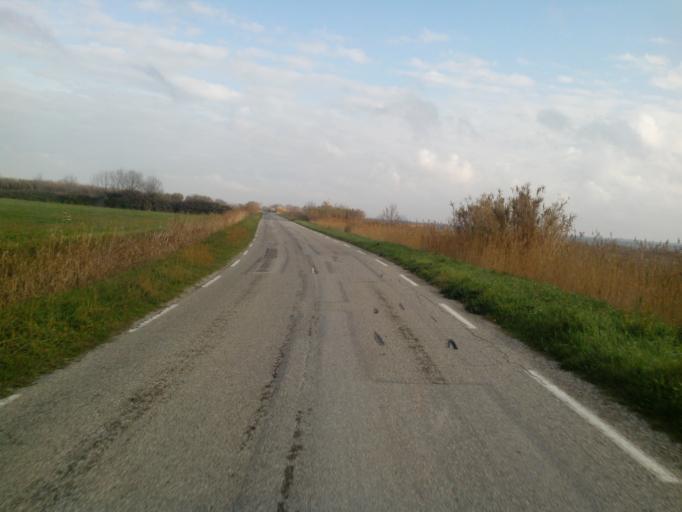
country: FR
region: Provence-Alpes-Cote d'Azur
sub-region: Departement des Bouches-du-Rhone
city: Arles
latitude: 43.5656
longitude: 4.5777
